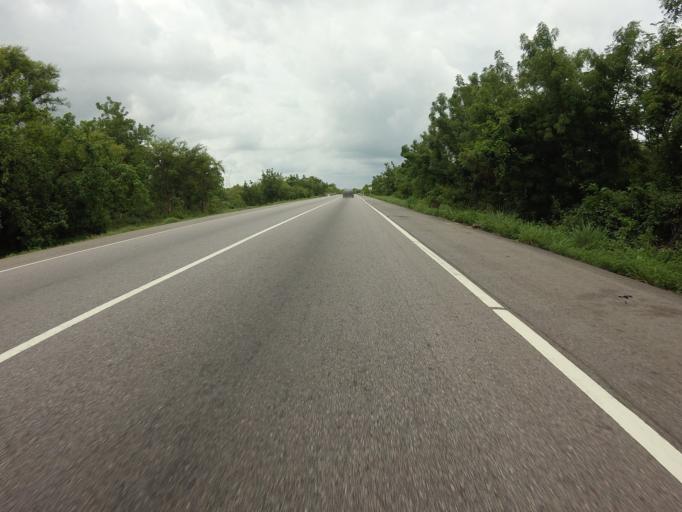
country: GH
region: Northern
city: Tamale
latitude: 8.8928
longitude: -1.4177
